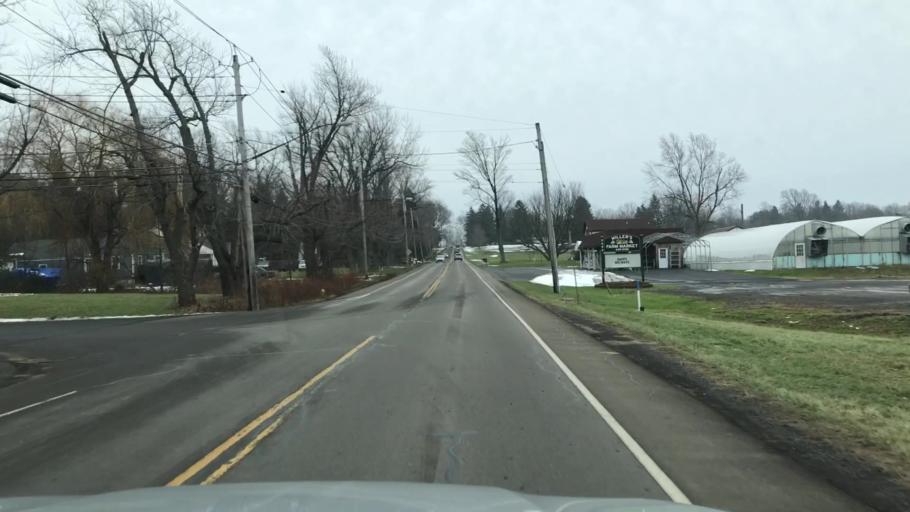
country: US
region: New York
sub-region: Erie County
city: Hamburg
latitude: 42.7449
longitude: -78.8040
